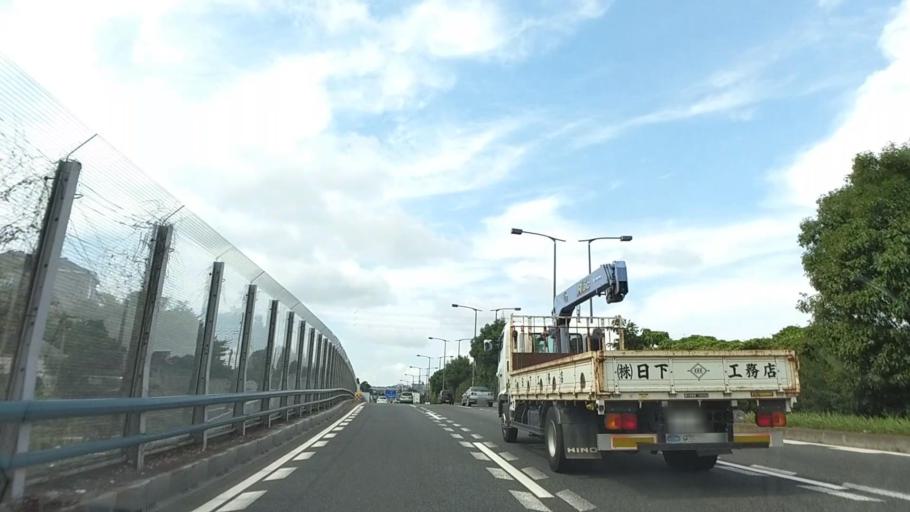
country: JP
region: Kanagawa
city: Yokohama
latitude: 35.4667
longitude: 139.5657
